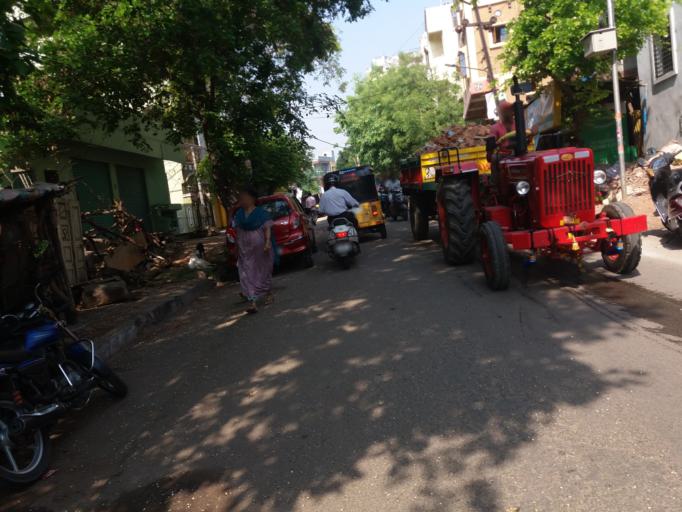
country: IN
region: Telangana
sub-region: Hyderabad
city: Malkajgiri
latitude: 17.4162
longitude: 78.5078
